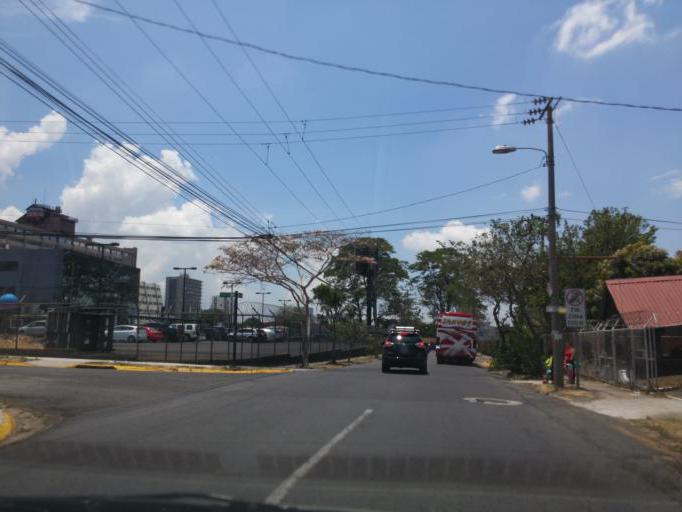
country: CR
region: San Jose
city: San Jose
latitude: 9.9407
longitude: -84.0971
